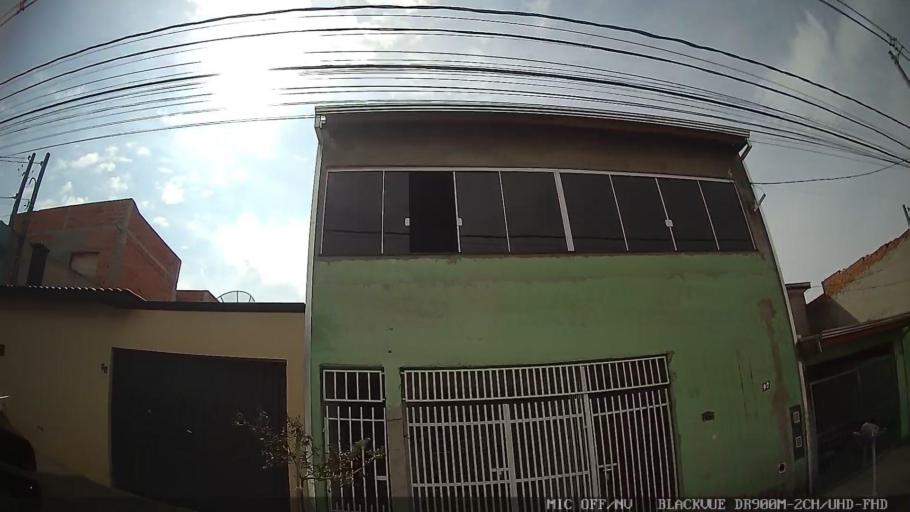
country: BR
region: Sao Paulo
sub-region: Indaiatuba
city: Indaiatuba
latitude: -23.1262
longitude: -47.2490
